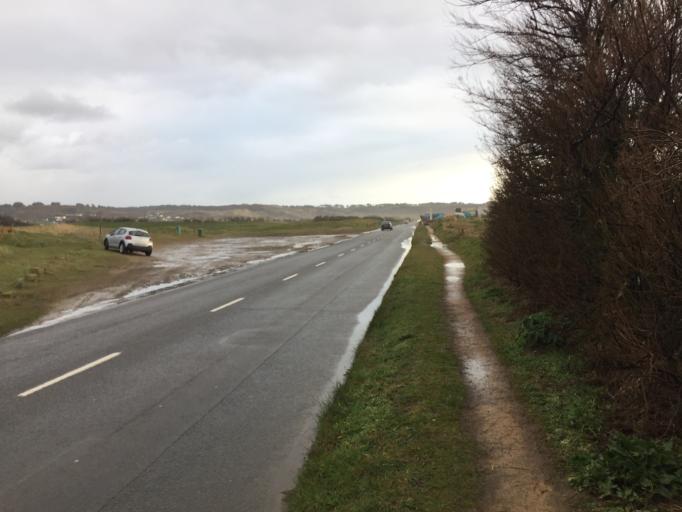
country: JE
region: St Helier
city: Saint Helier
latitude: 49.2122
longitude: -2.2242
